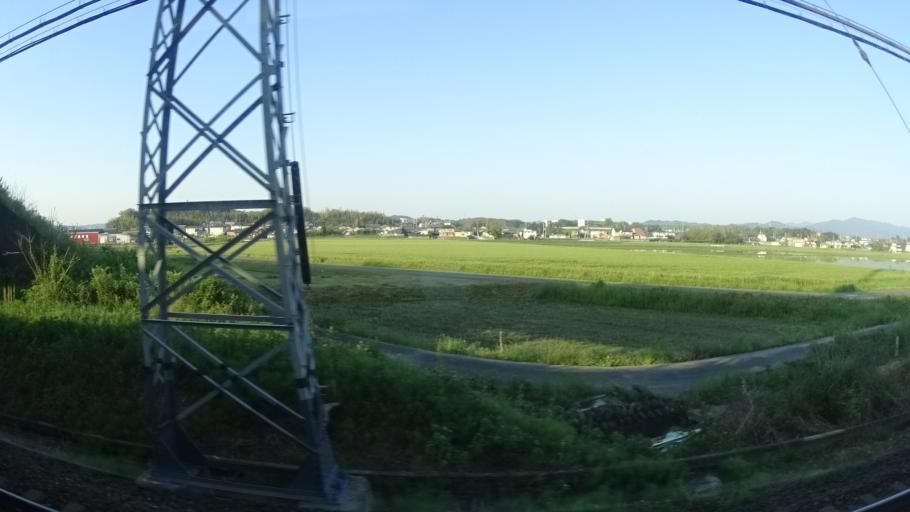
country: JP
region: Mie
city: Ise
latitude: 34.5521
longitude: 136.5753
